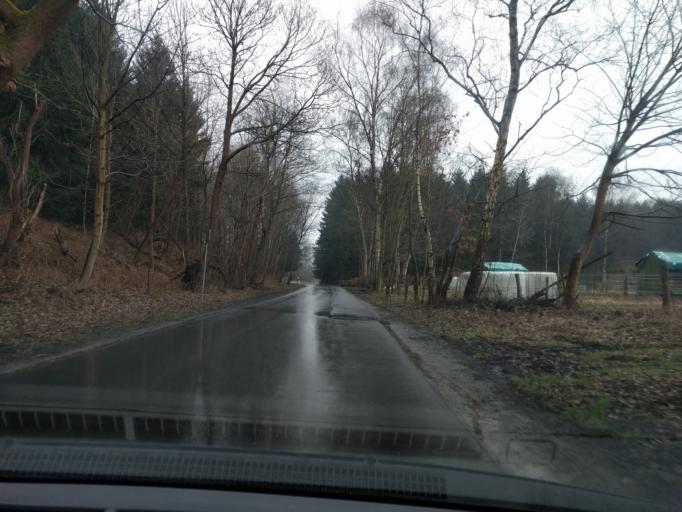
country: DE
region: Lower Saxony
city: Bendestorf
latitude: 53.3636
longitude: 9.9620
